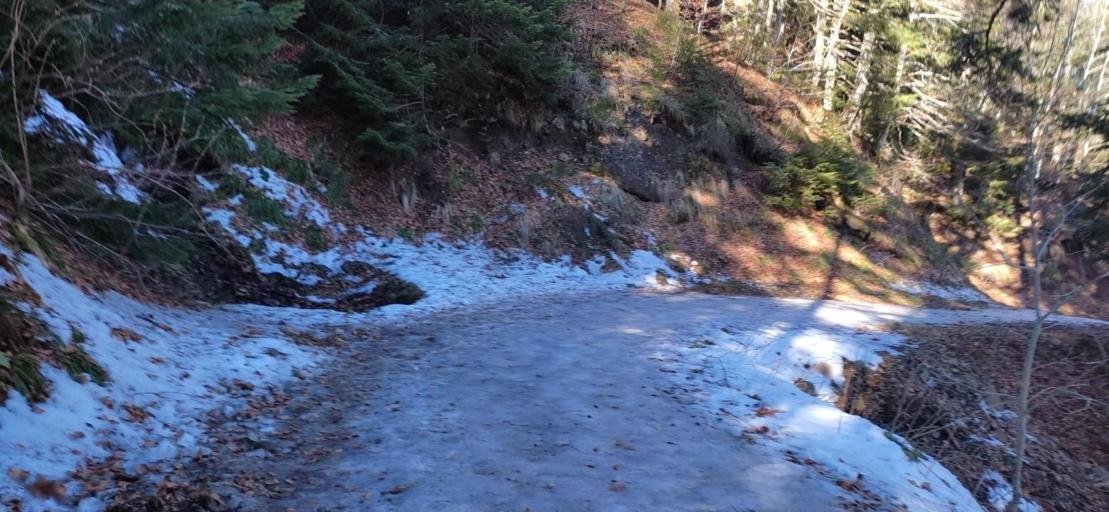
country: FR
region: Auvergne
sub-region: Departement du Puy-de-Dome
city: Mont-Dore
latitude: 45.5572
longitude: 2.8101
